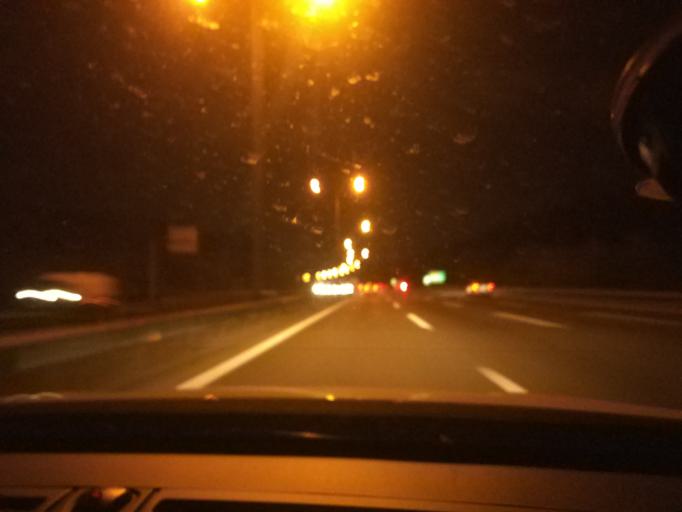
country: TR
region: Istanbul
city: Umraniye
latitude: 41.0847
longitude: 29.0942
